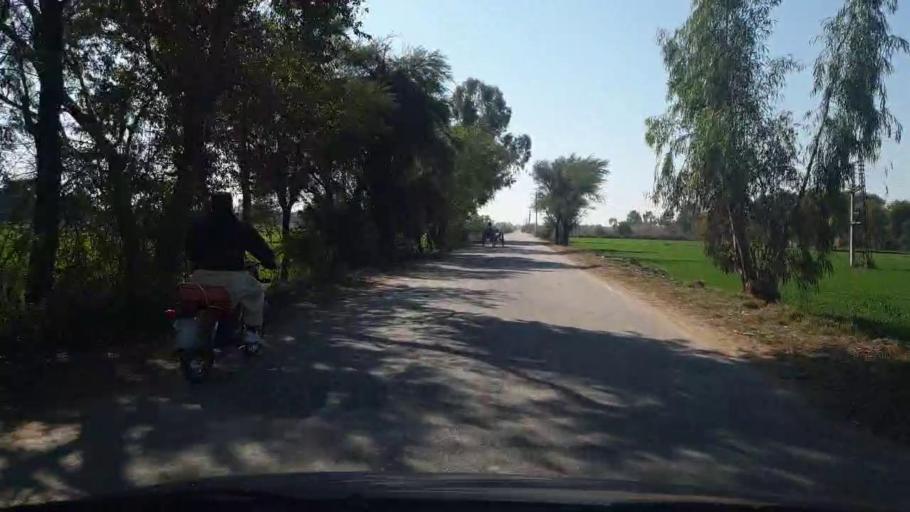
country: PK
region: Sindh
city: Bozdar
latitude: 27.0849
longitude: 68.6218
